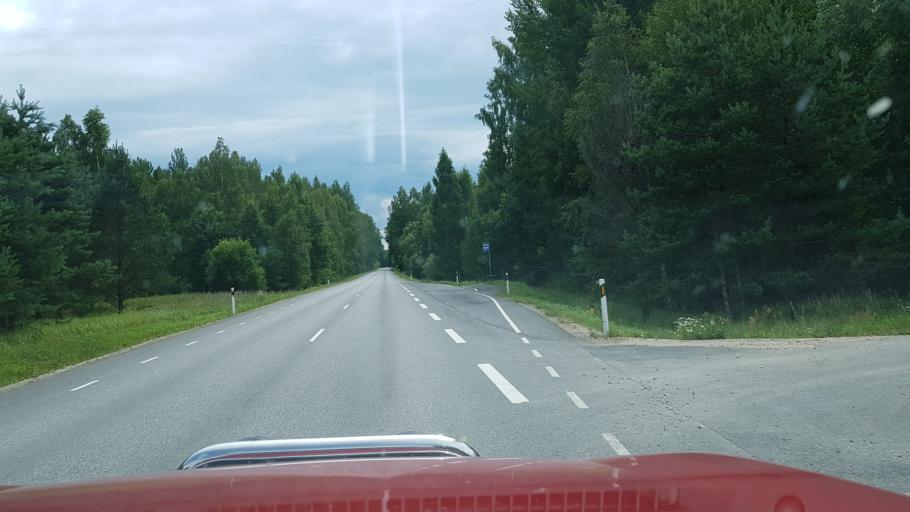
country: EE
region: Polvamaa
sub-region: Raepina vald
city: Rapina
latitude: 58.0539
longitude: 27.5537
